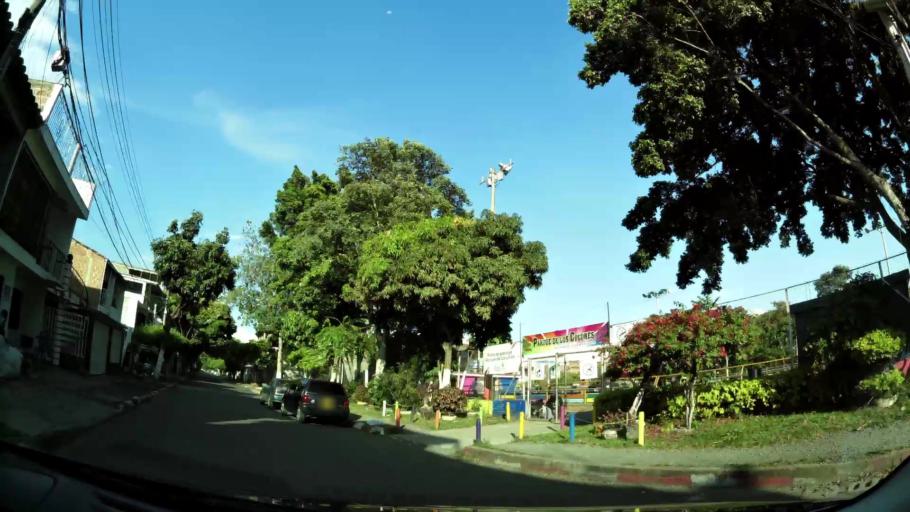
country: CO
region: Valle del Cauca
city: Cali
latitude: 3.4136
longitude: -76.5125
